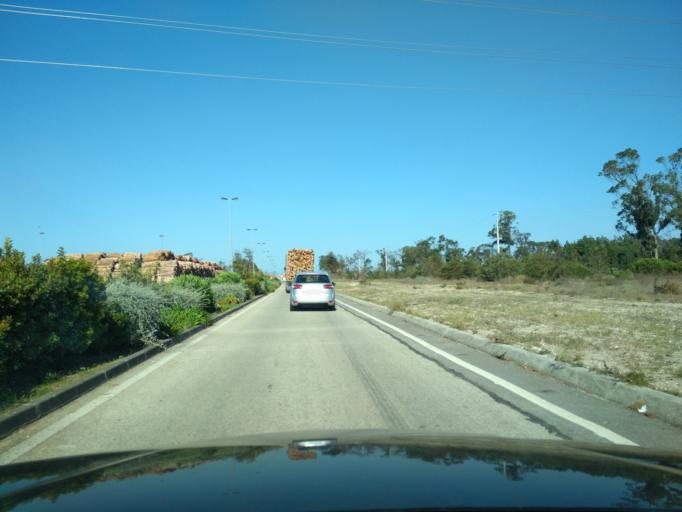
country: PT
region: Coimbra
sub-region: Figueira da Foz
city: Lavos
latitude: 40.0546
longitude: -8.8754
